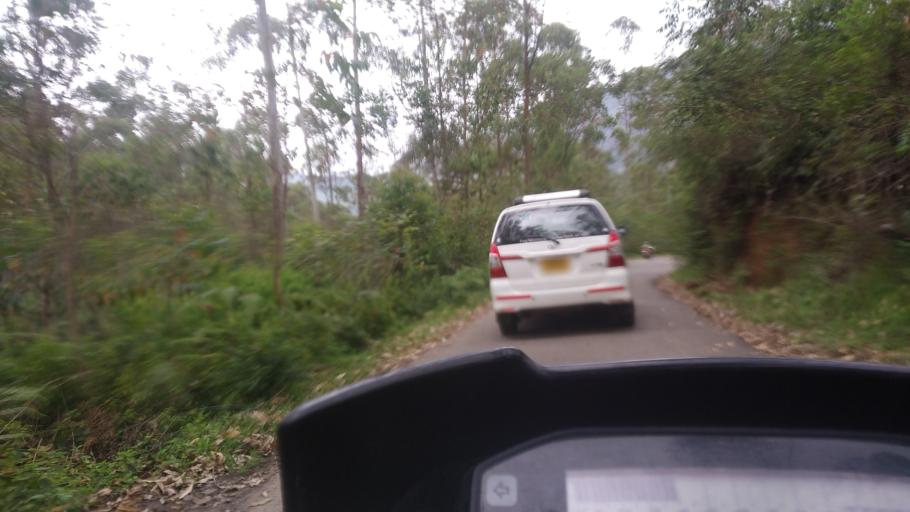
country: IN
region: Kerala
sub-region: Idukki
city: Munnar
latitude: 10.0602
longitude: 77.1076
